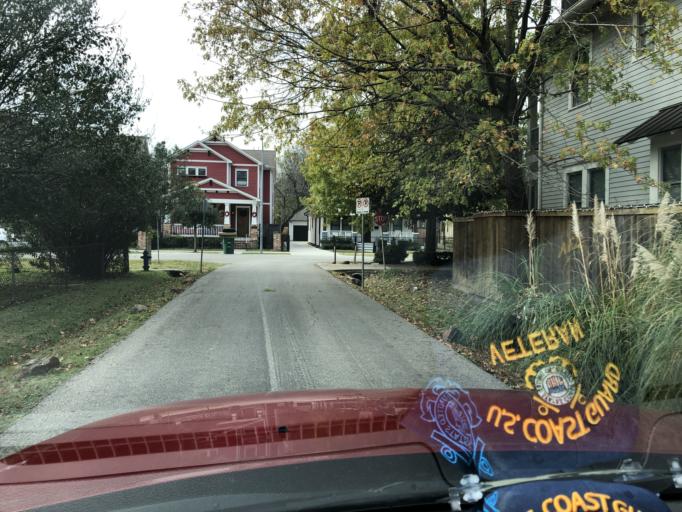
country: US
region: Texas
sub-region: Harris County
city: Houston
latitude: 29.7898
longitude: -95.3996
